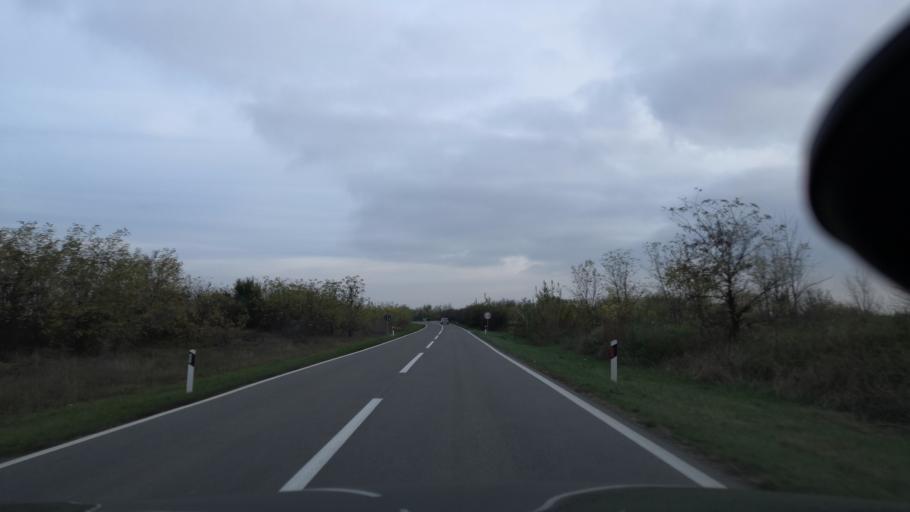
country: RS
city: Sanad
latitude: 45.9677
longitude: 20.1249
